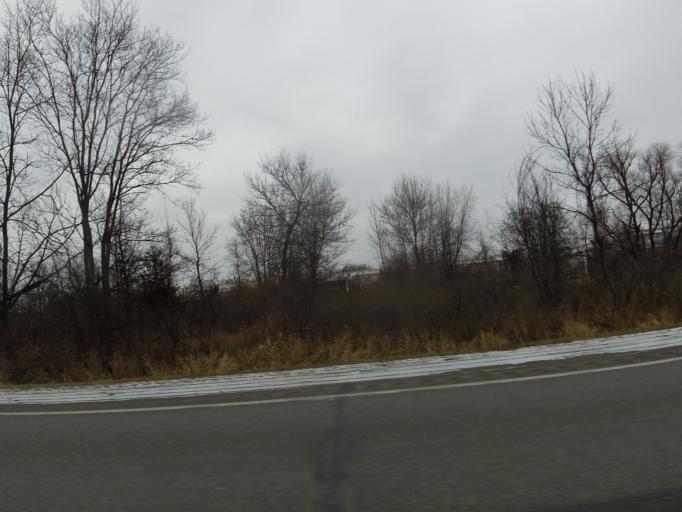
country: US
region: Minnesota
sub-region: Hennepin County
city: Independence
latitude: 45.0130
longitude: -93.6906
